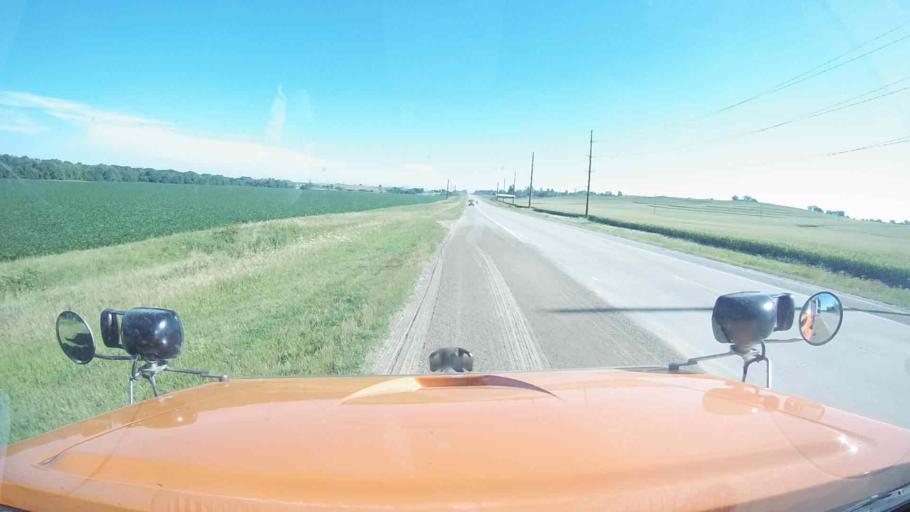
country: US
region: Iowa
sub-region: Iowa County
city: North English
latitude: 41.5725
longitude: -92.0653
